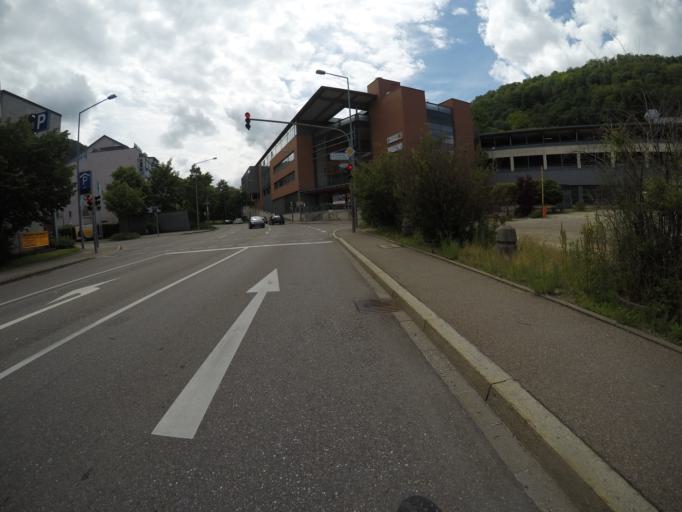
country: DE
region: Baden-Wuerttemberg
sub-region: Regierungsbezirk Stuttgart
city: Geislingen an der Steige
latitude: 48.6124
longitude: 9.8420
